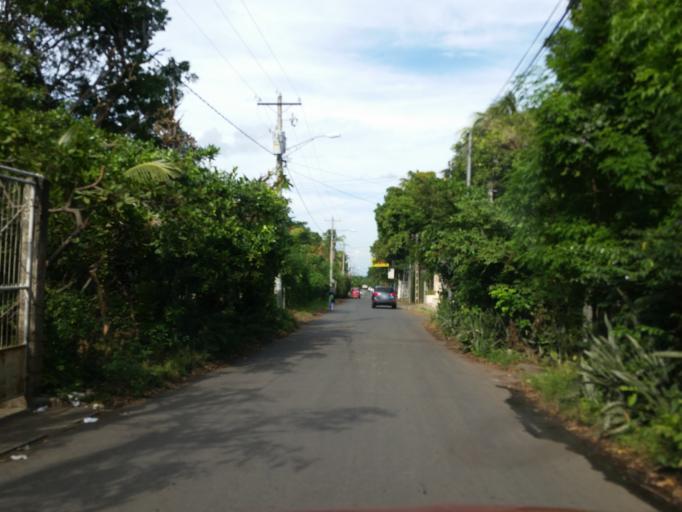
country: NI
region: Managua
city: Managua
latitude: 12.0879
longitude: -86.2310
